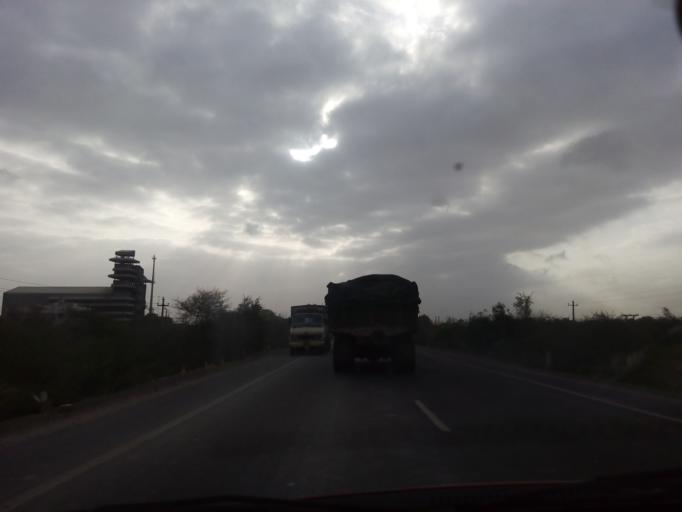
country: IN
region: Gujarat
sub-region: Kachchh
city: Bhuj
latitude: 23.2371
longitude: 69.7942
